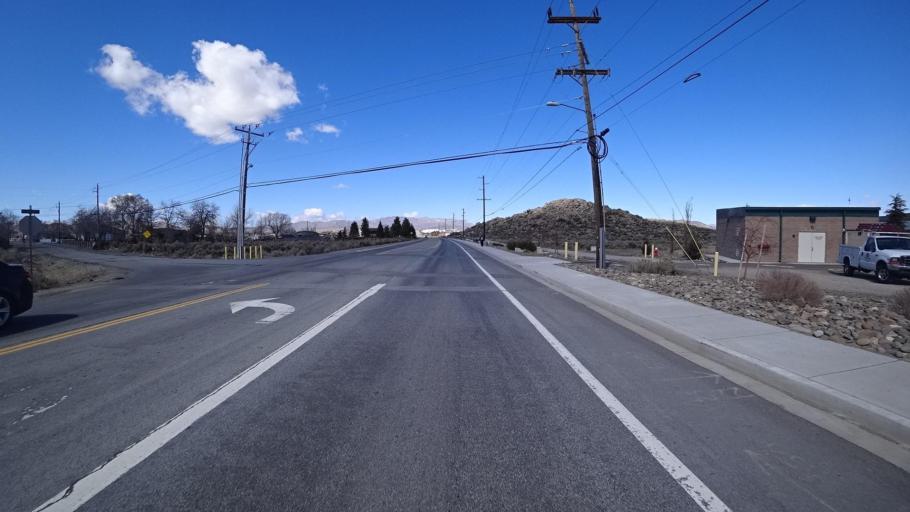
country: US
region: Nevada
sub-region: Washoe County
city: Lemmon Valley
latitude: 39.6316
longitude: -119.8535
